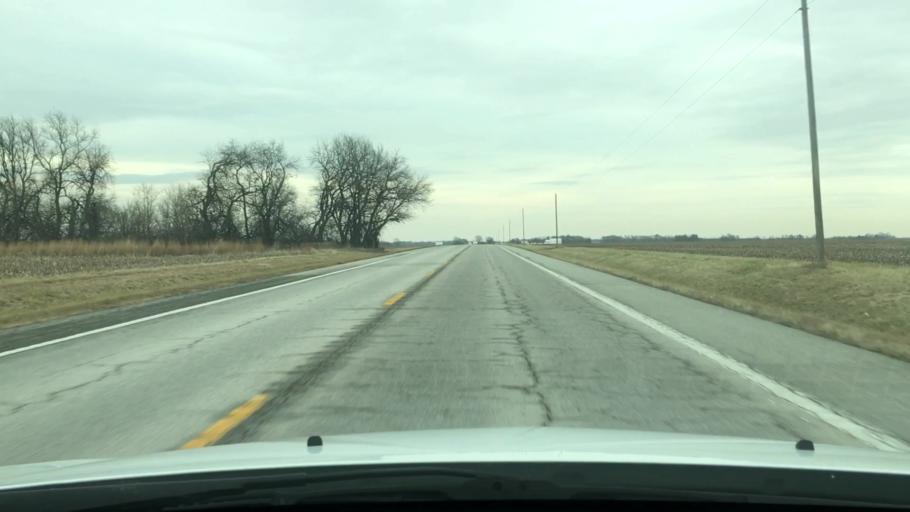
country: US
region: Missouri
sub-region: Audrain County
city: Vandalia
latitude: 39.2809
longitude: -91.6359
